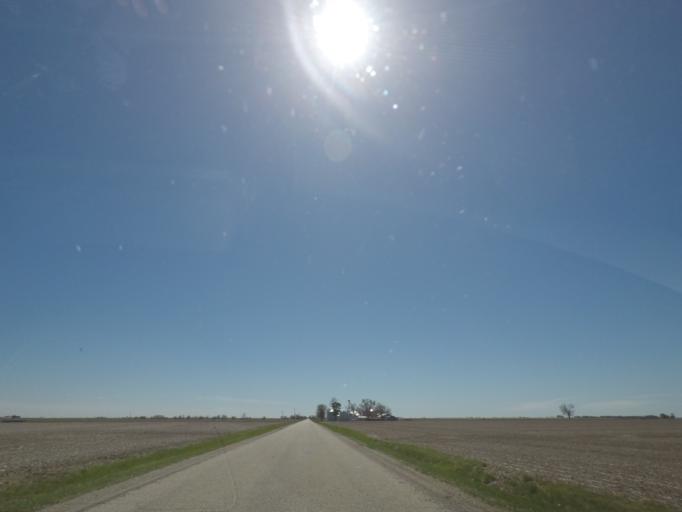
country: US
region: Illinois
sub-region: Logan County
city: Atlanta
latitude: 40.2034
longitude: -89.1943
